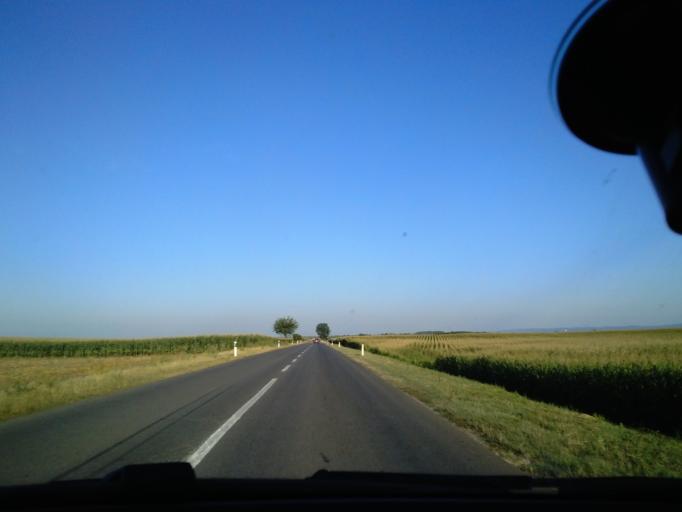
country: RS
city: Maglic
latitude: 45.3878
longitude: 19.4956
